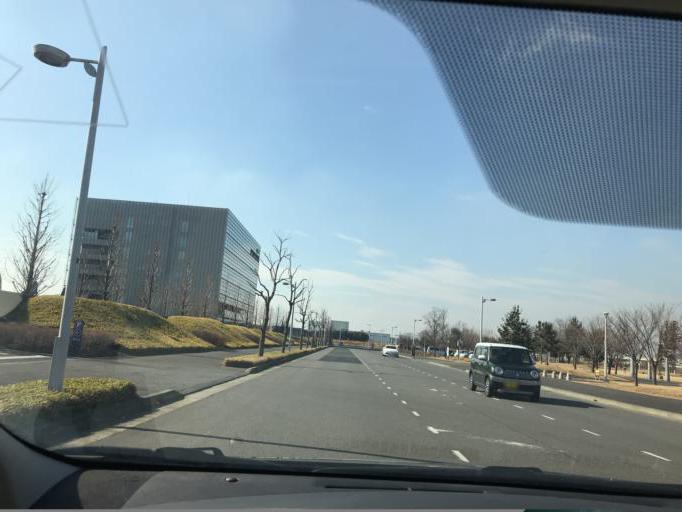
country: JP
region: Ibaraki
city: Naka
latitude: 36.0795
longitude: 140.0820
